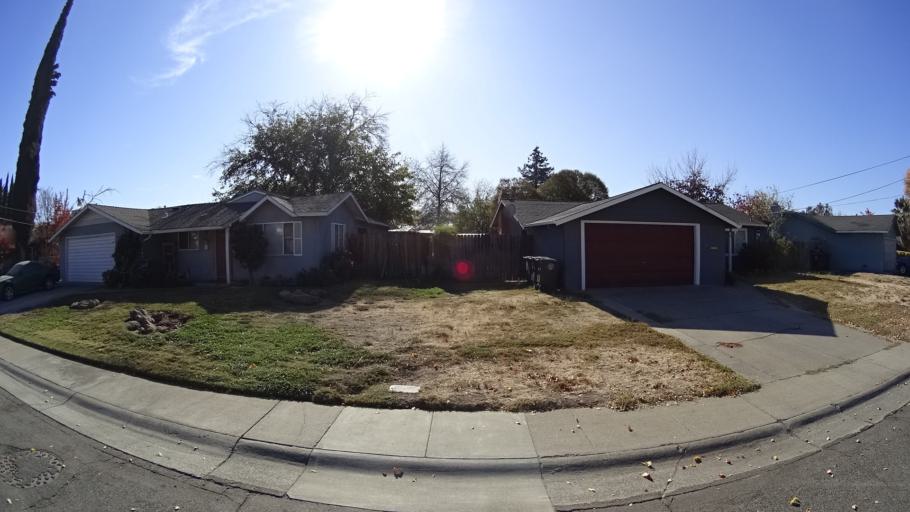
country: US
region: California
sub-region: Sacramento County
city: Antelope
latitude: 38.6878
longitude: -121.3147
